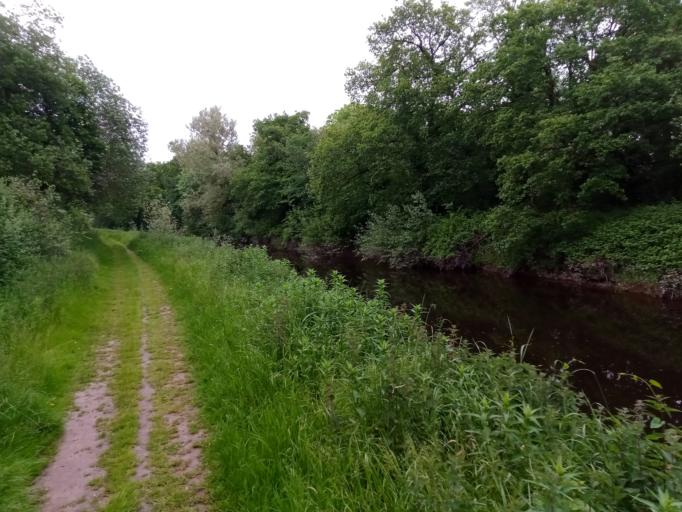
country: IE
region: Leinster
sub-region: County Carlow
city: Carlow
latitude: 52.8165
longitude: -6.9512
